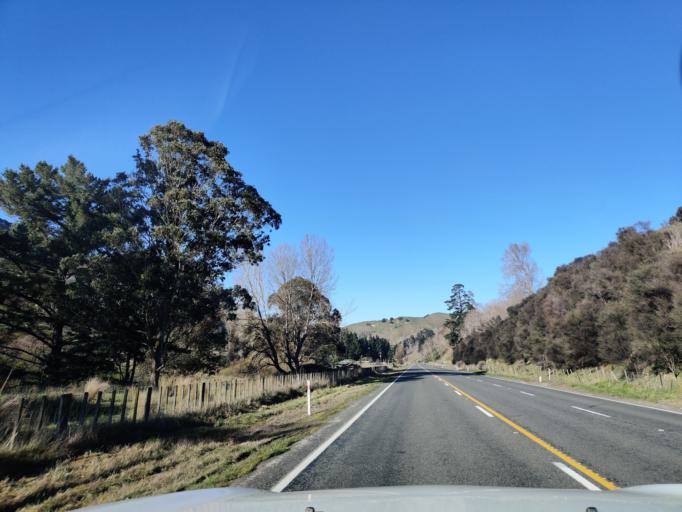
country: NZ
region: Manawatu-Wanganui
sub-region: Ruapehu District
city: Waiouru
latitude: -39.7833
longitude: 175.7862
